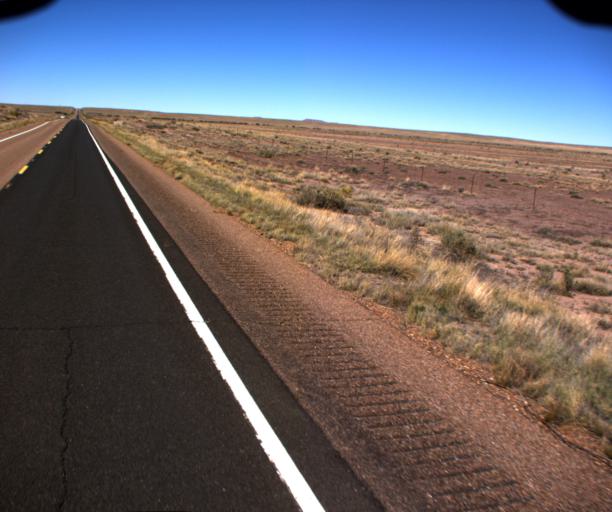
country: US
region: Arizona
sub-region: Navajo County
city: Snowflake
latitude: 34.7320
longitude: -109.7836
